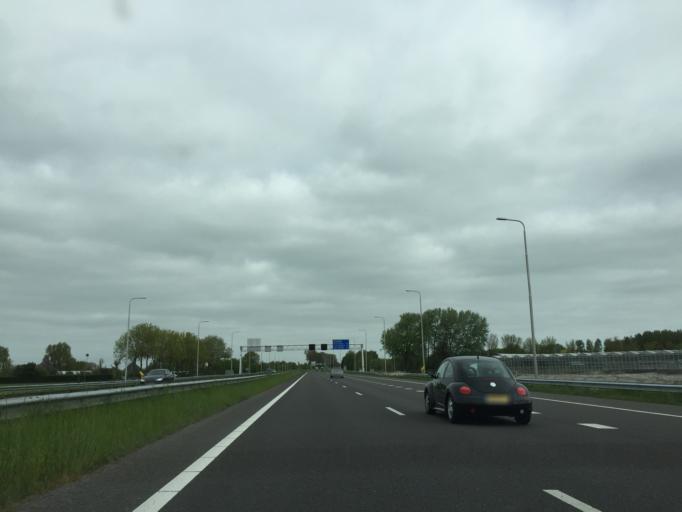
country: NL
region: North Holland
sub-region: Gemeente Hoorn
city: Hoorn
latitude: 52.6702
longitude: 5.0331
